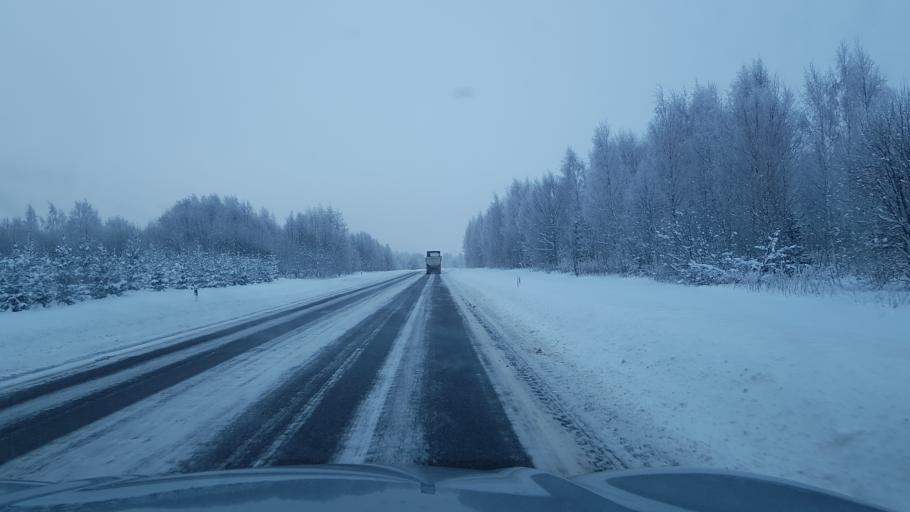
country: EE
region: Ida-Virumaa
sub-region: Johvi vald
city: Johvi
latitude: 59.2165
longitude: 27.3389
